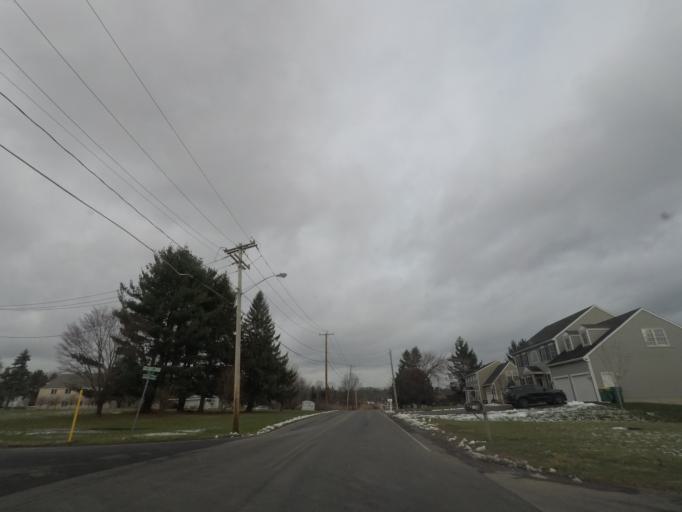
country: US
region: New York
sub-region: Rensselaer County
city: East Greenbush
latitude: 42.5857
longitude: -73.7143
